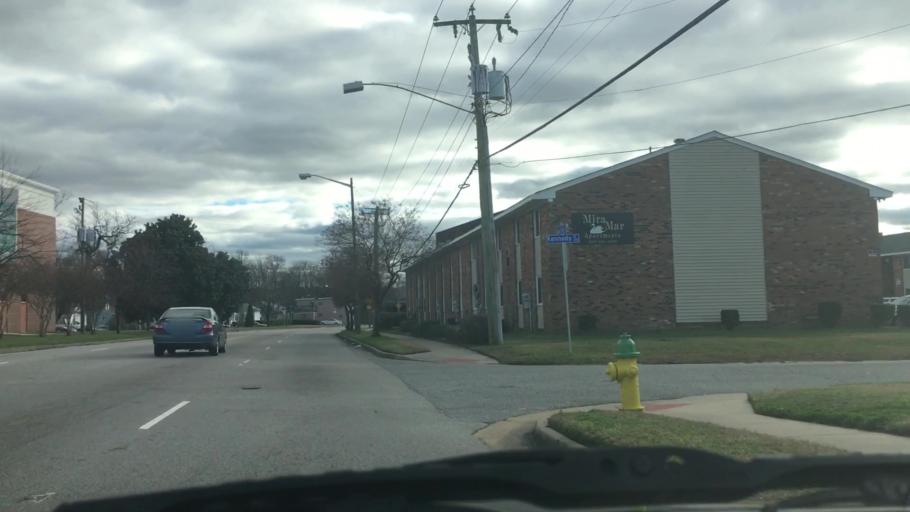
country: US
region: Virginia
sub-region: City of Norfolk
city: Norfolk
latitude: 36.9057
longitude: -76.2435
